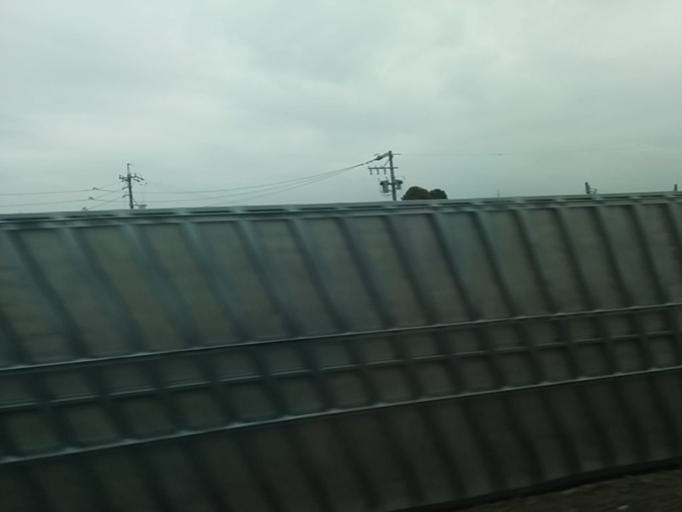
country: JP
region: Aichi
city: Anjo
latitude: 34.9335
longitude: 137.0930
